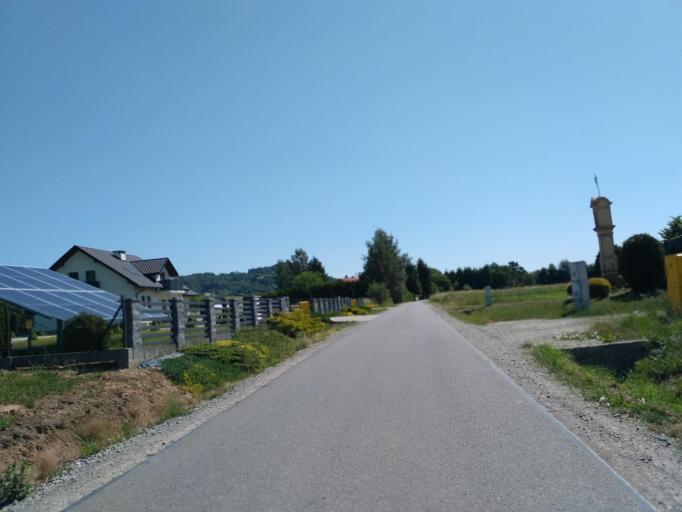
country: PL
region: Subcarpathian Voivodeship
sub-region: Powiat krosnienski
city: Odrzykon
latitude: 49.7251
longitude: 21.7660
